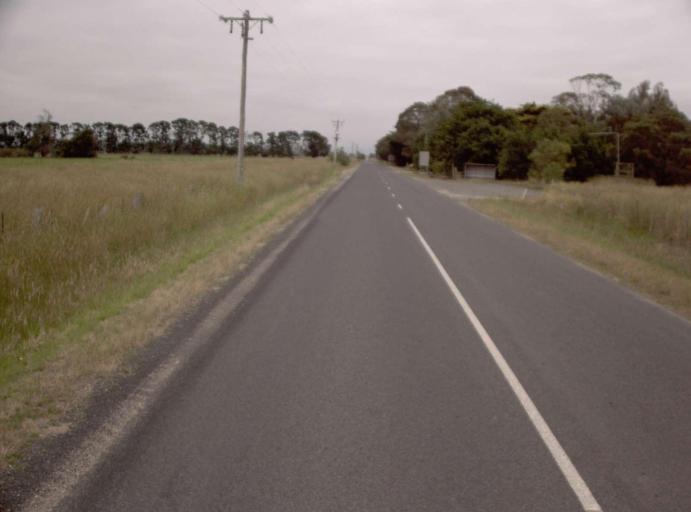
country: AU
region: Victoria
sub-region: Wellington
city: Heyfield
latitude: -38.0259
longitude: 146.8784
